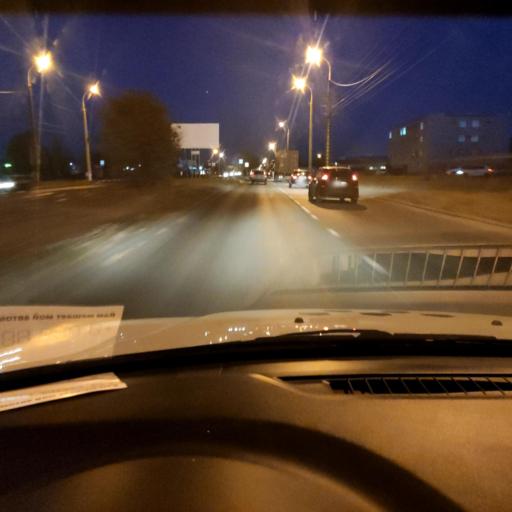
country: RU
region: Samara
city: Tol'yatti
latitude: 53.5594
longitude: 49.3099
